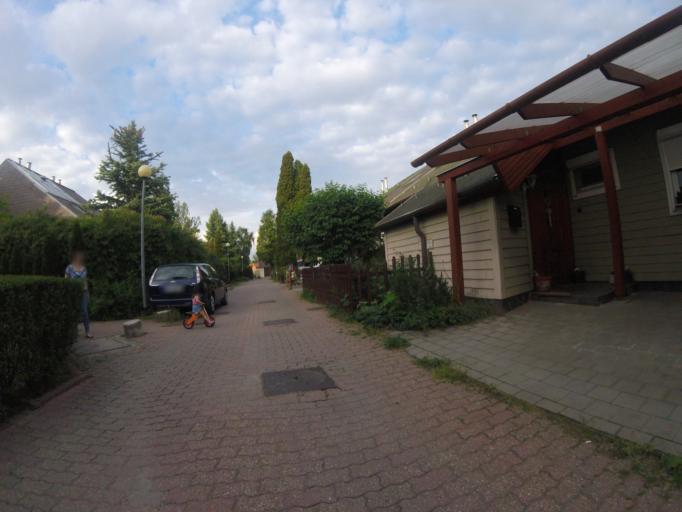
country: HU
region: Budapest
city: Budapest III. keruelet
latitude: 47.5622
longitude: 19.0464
